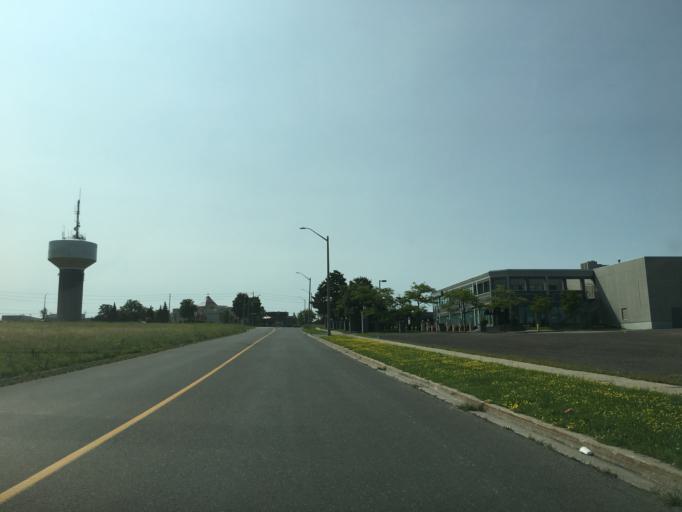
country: CA
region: Ontario
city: Markham
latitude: 43.8443
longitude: -79.3119
